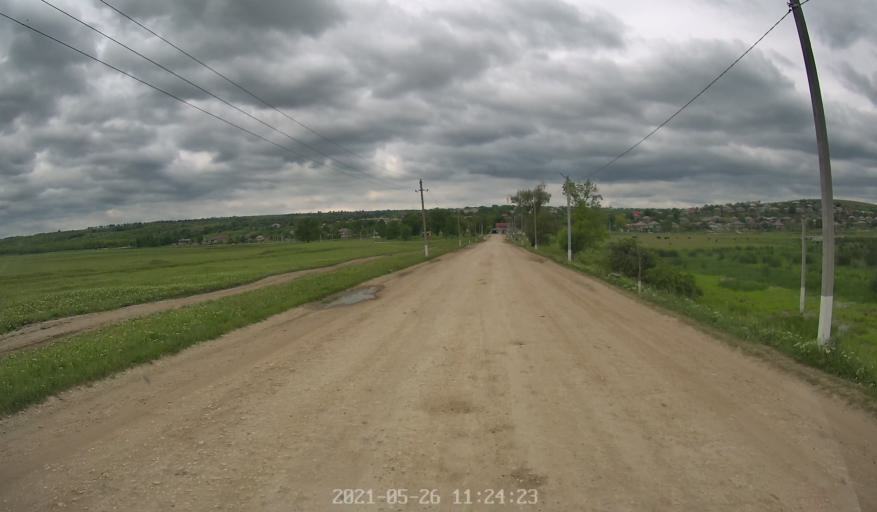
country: MD
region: Hincesti
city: Dancu
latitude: 46.8242
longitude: 28.3742
